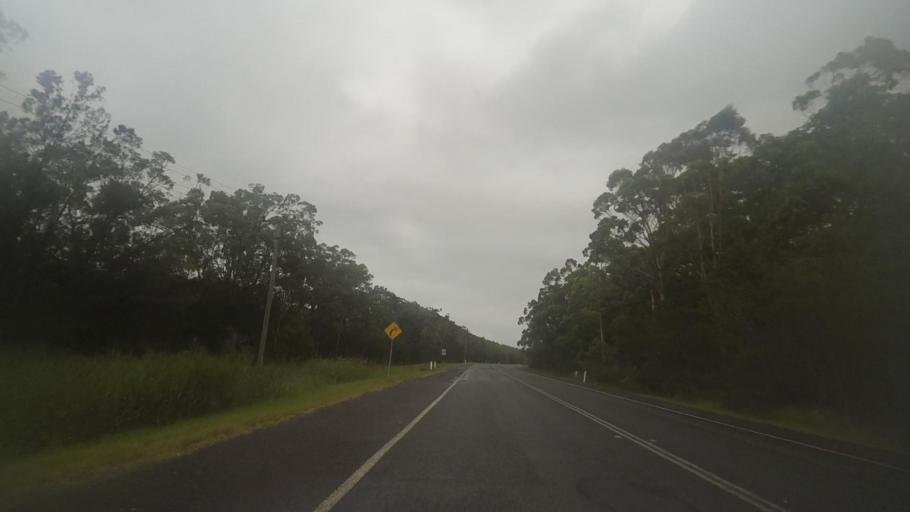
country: AU
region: New South Wales
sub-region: Port Stephens Shire
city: Port Stephens
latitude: -32.6360
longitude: 151.9950
